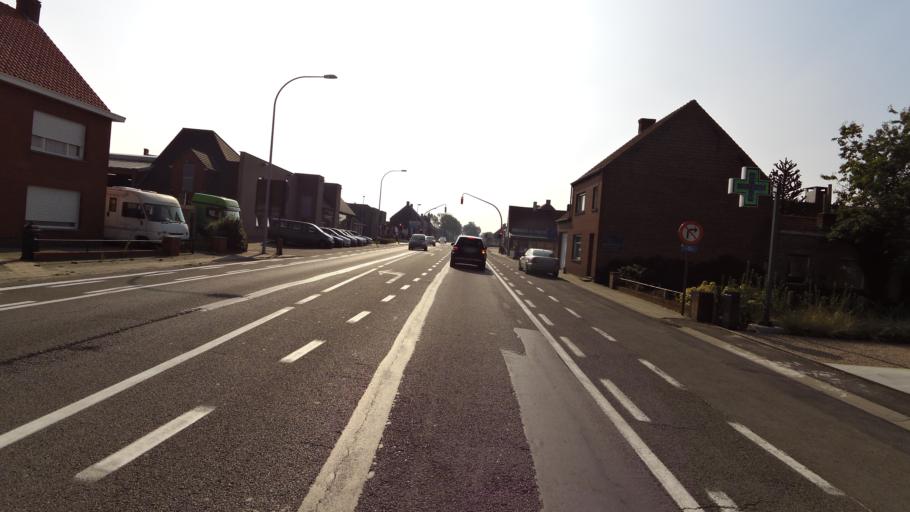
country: BE
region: Flanders
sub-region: Provincie West-Vlaanderen
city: Ichtegem
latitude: 51.1020
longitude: 3.0309
